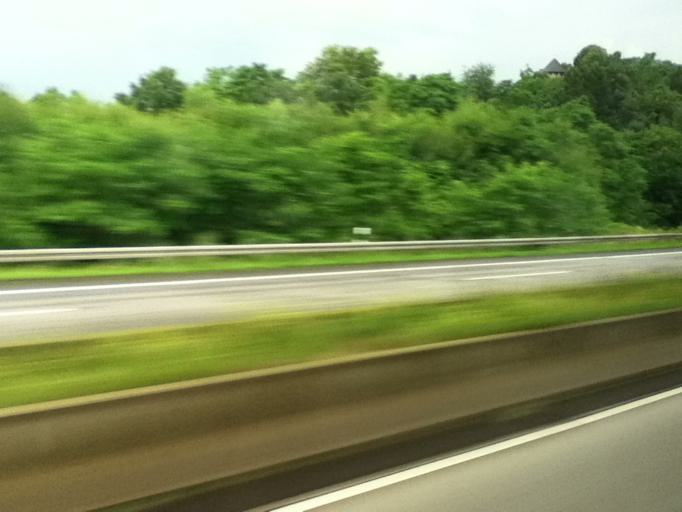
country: DE
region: Hesse
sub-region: Regierungsbezirk Giessen
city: Grunberg
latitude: 50.6260
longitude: 8.9041
